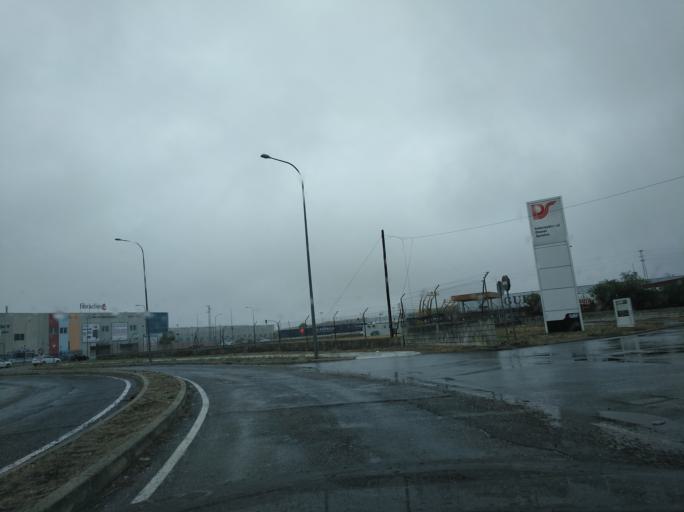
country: ES
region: Extremadura
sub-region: Provincia de Badajoz
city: Badajoz
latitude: 38.8979
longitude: -6.9904
